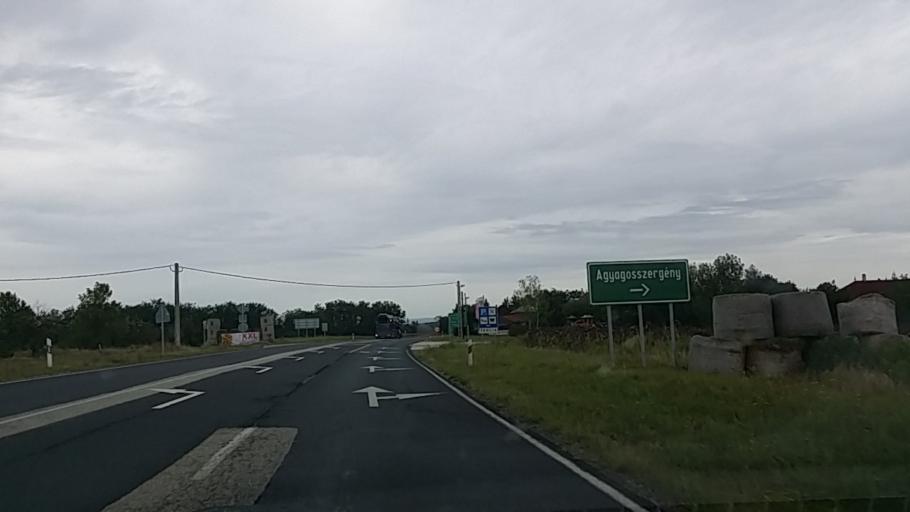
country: HU
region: Gyor-Moson-Sopron
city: Fertoszentmiklos
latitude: 47.5968
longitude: 16.9215
